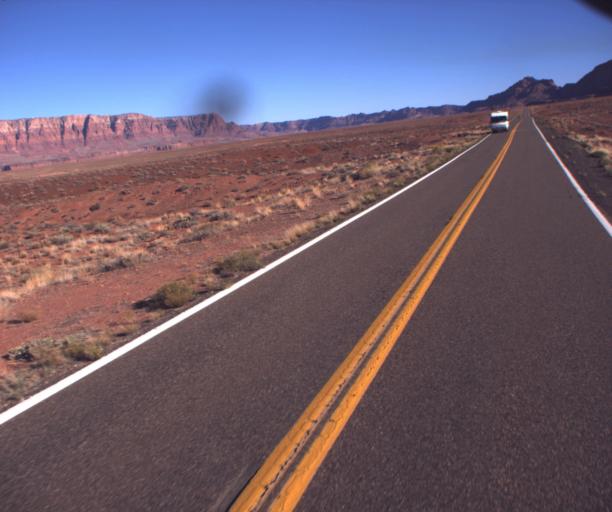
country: US
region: Arizona
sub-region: Coconino County
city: LeChee
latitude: 36.7561
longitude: -111.6308
